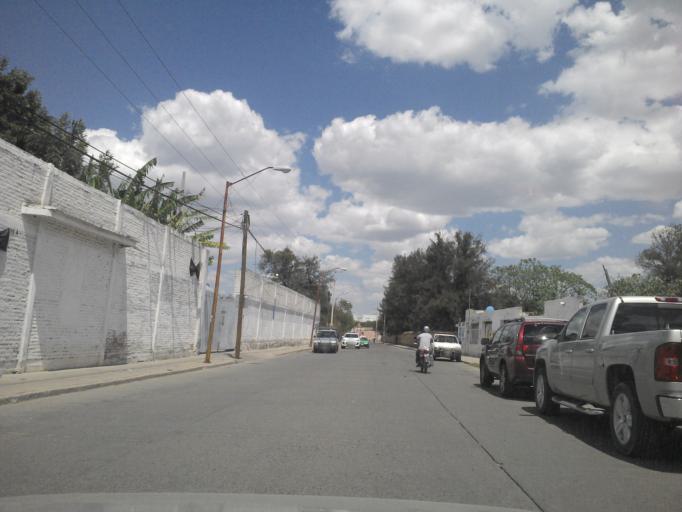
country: MX
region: Guanajuato
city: San Francisco del Rincon
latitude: 21.0227
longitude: -101.8661
